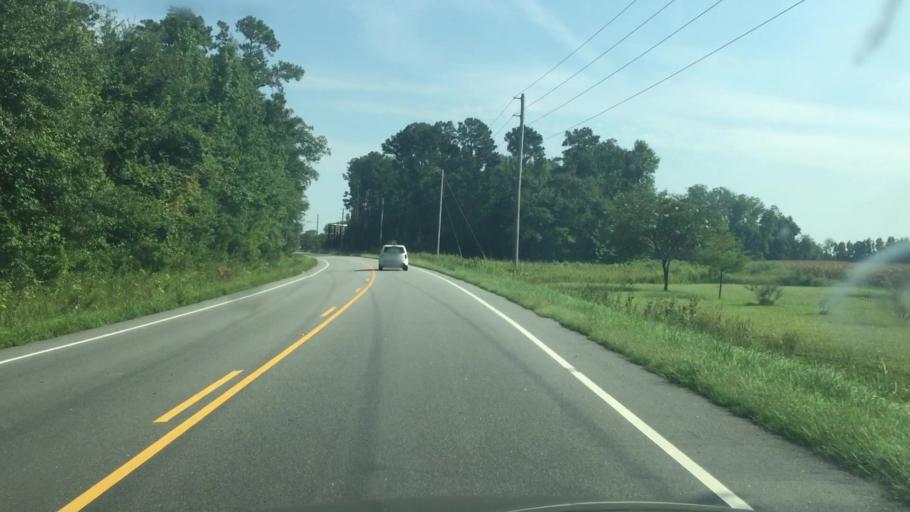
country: US
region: North Carolina
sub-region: Columbus County
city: Tabor City
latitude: 34.2159
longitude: -78.8241
